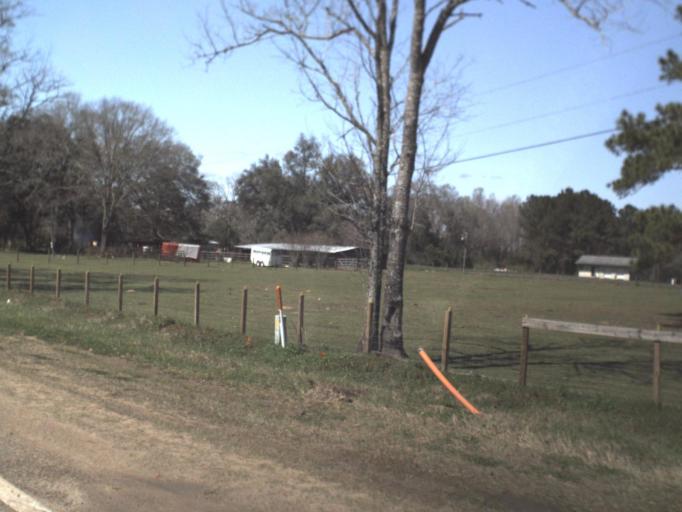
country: US
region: Florida
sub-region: Gadsden County
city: Quincy
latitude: 30.5897
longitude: -84.6258
